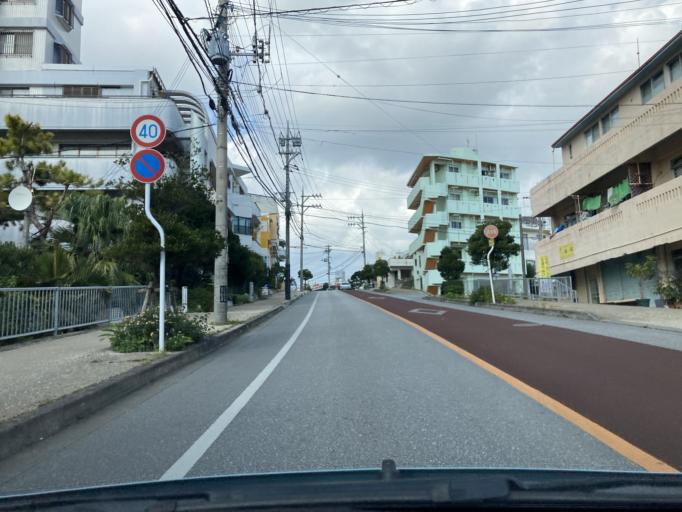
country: JP
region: Okinawa
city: Ginowan
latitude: 26.2443
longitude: 127.7261
